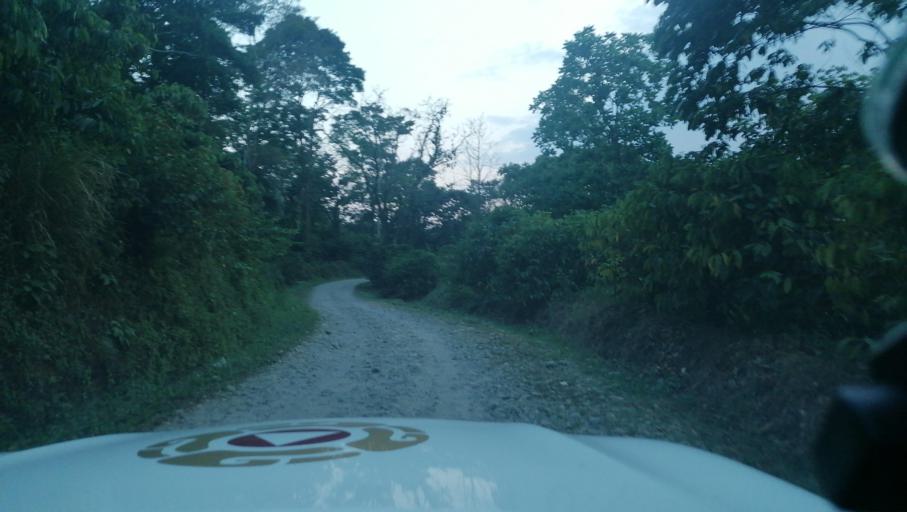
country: MX
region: Chiapas
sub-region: Cacahoatan
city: Benito Juarez
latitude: 15.0623
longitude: -92.2399
